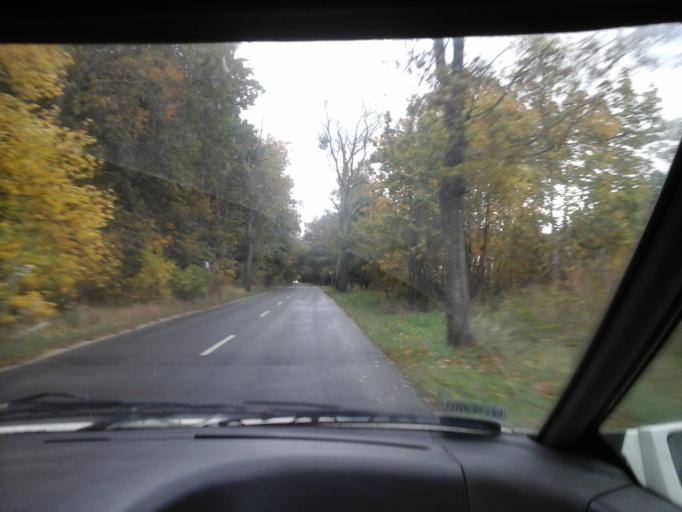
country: PL
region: Pomeranian Voivodeship
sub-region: Powiat gdanski
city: Cedry Wielkie
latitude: 54.3425
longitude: 18.8566
